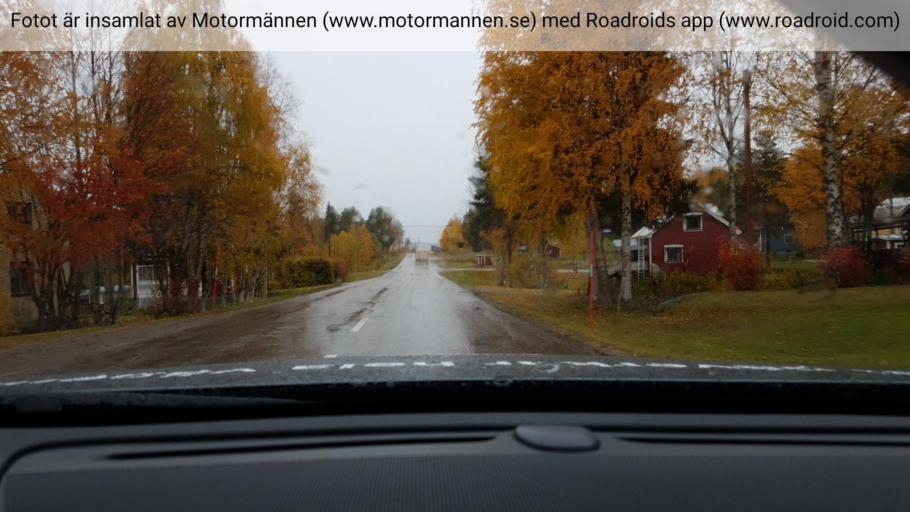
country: SE
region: Norrbotten
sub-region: Overkalix Kommun
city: OEverkalix
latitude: 66.7880
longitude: 22.9172
